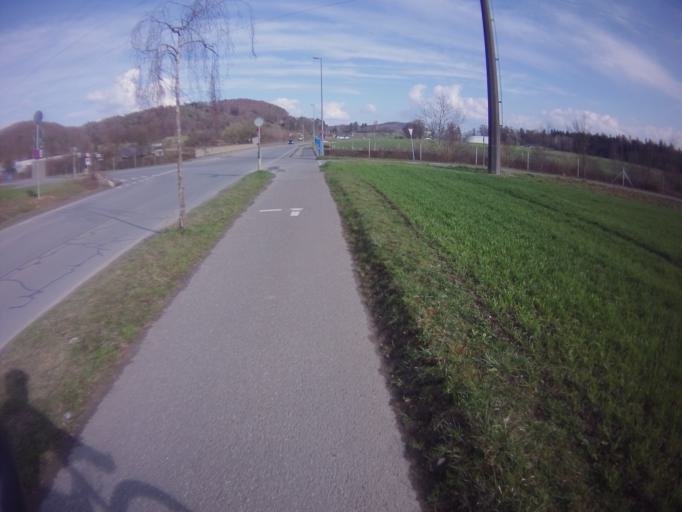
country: CH
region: Aargau
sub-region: Bezirk Baden
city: Neuenhof
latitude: 47.4514
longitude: 8.3442
